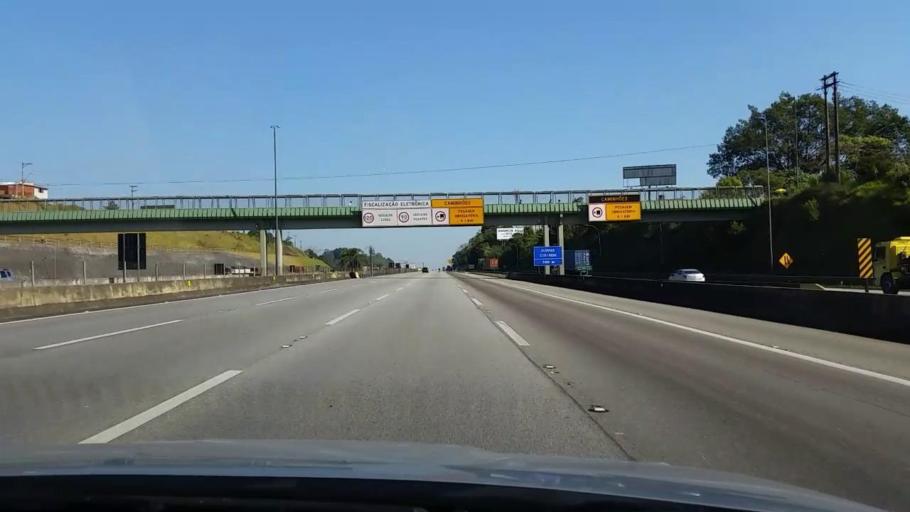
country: BR
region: Sao Paulo
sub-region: Sao Bernardo Do Campo
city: Sao Bernardo do Campo
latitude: -23.7707
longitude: -46.5930
